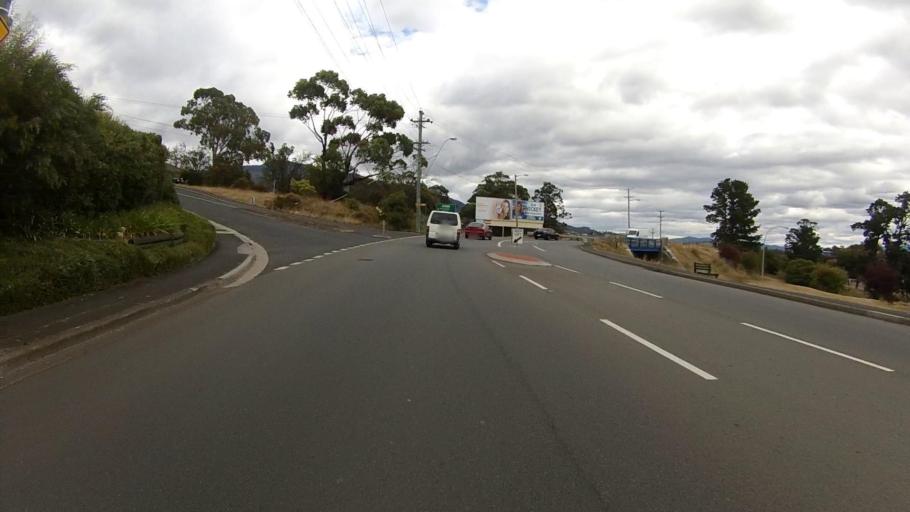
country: AU
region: Tasmania
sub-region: Glenorchy
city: Berriedale
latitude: -42.8204
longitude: 147.2616
